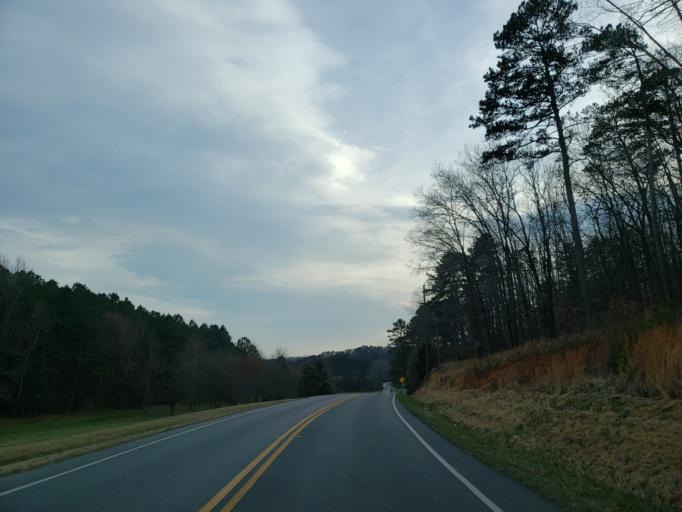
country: US
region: Georgia
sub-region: Whitfield County
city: Varnell
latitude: 34.9035
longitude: -84.9606
